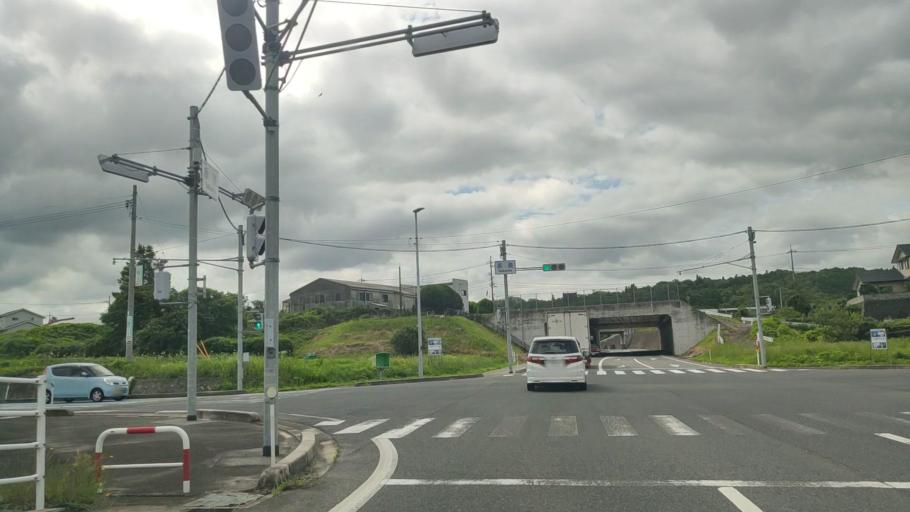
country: JP
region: Tottori
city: Yonago
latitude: 35.3835
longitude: 133.3870
